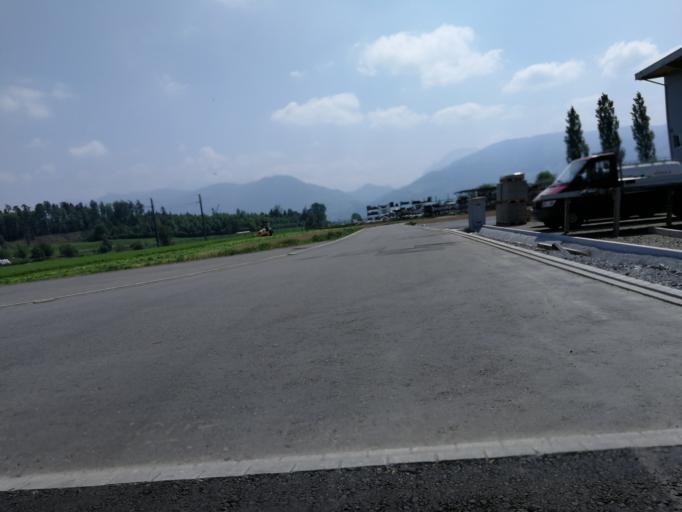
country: CH
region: Saint Gallen
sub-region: Wahlkreis See-Gaster
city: Jona
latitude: 47.2258
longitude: 8.8690
